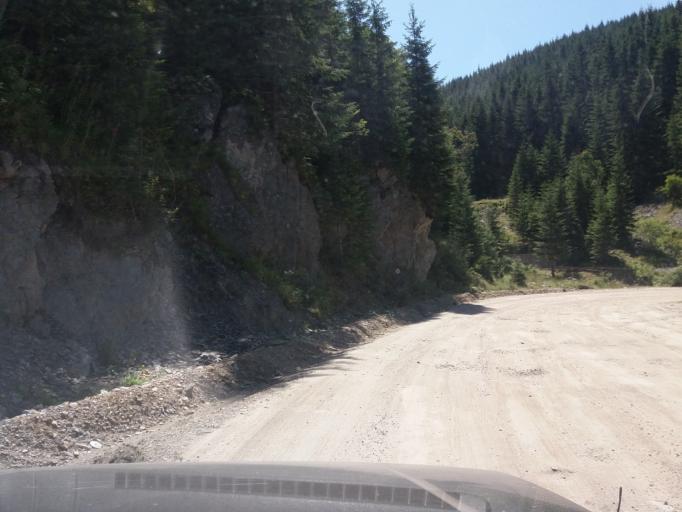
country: RO
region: Hunedoara
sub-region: Oras Petrila
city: Petrila
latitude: 45.4001
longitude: 23.5721
